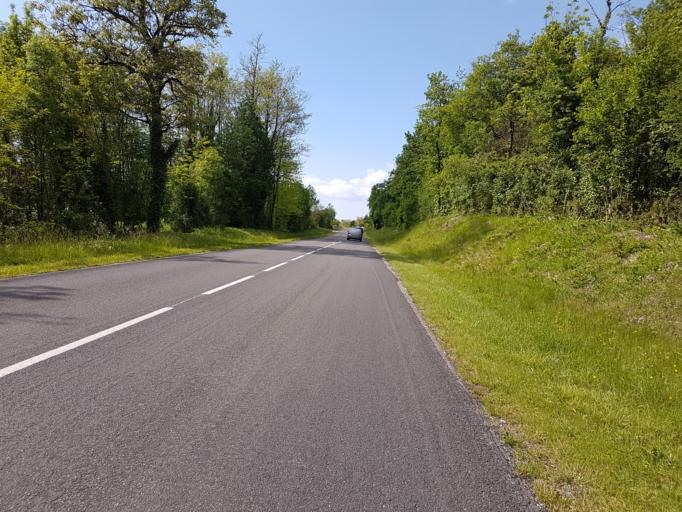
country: FR
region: Rhone-Alpes
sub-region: Departement de l'Isere
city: Bouvesse-Quirieu
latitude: 45.7858
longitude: 5.4655
